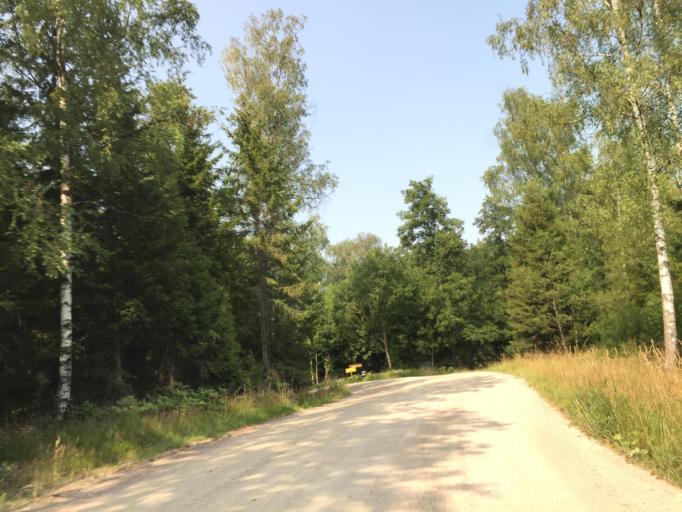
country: SE
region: Vaestra Goetaland
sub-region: Lilla Edets Kommun
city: Lilla Edet
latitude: 58.2352
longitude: 12.1110
